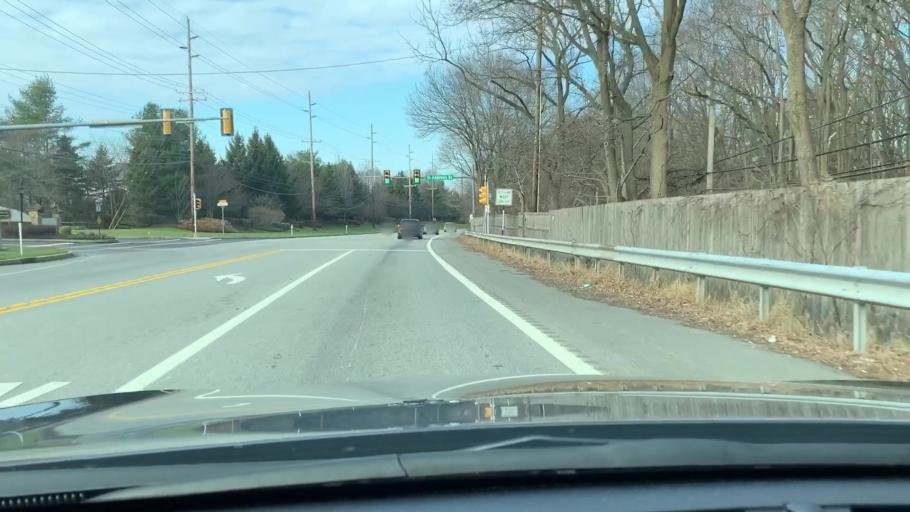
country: US
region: Pennsylvania
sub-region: Chester County
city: Paoli
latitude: 40.0230
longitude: -75.4585
